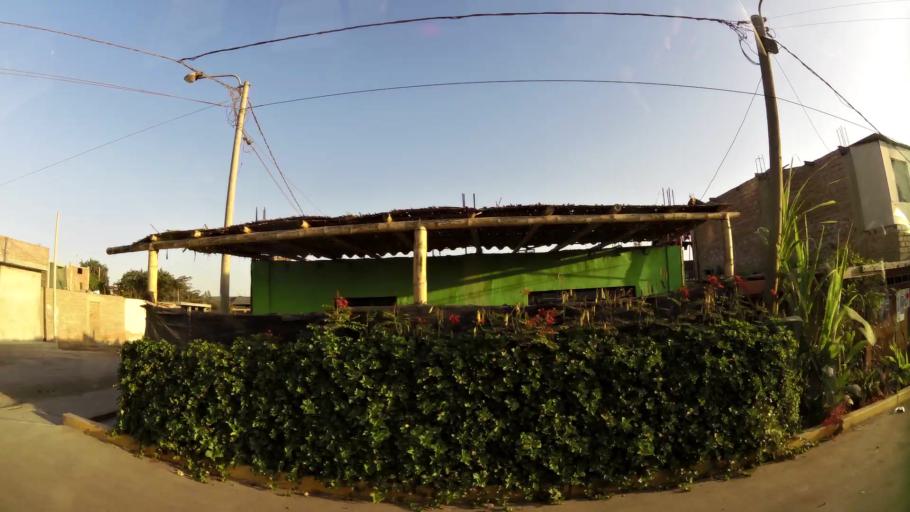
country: PE
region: Ica
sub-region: Provincia de Pisco
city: Villa Tupac Amaru
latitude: -13.7072
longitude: -76.1501
